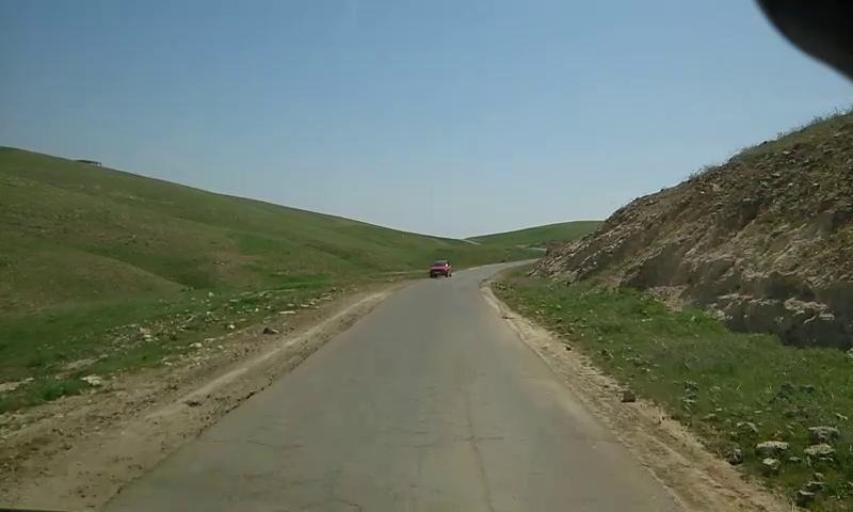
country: PS
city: `Arab ar Rashaydah
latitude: 31.5538
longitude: 35.2498
